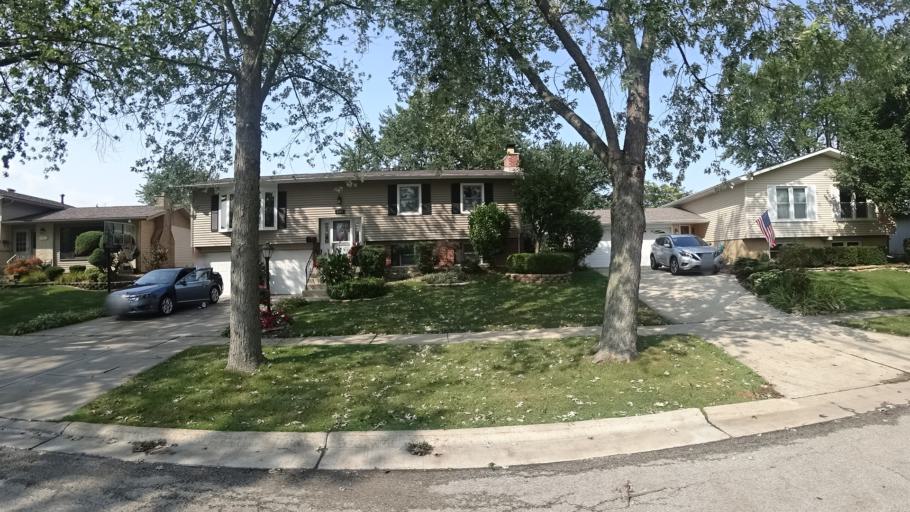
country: US
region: Illinois
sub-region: Cook County
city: Oak Forest
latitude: 41.6131
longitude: -87.7726
